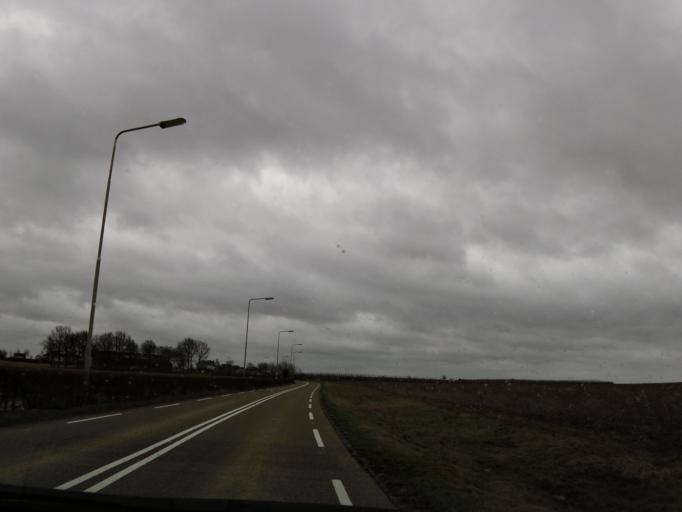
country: NL
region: Limburg
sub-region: Valkenburg aan de Geul
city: Sibbe
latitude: 50.8510
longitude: 5.8146
